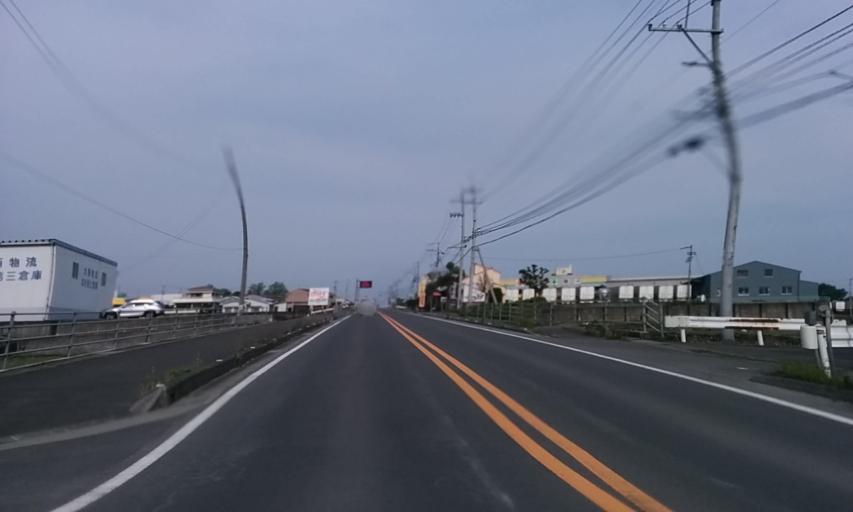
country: JP
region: Ehime
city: Kawanoecho
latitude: 33.9670
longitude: 133.4863
